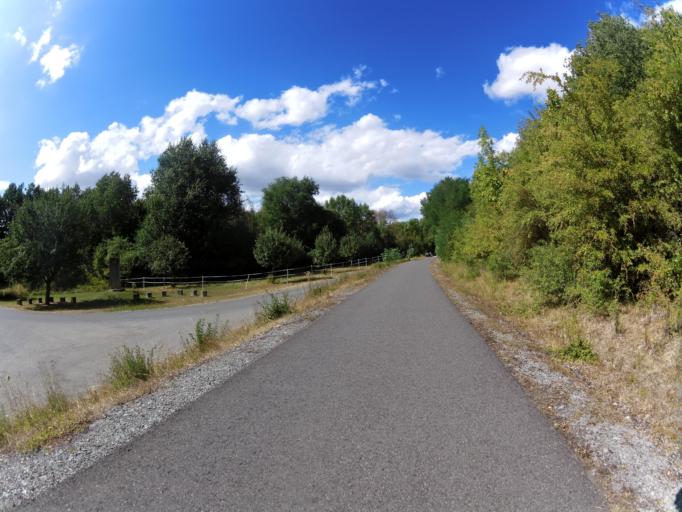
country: DE
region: Bavaria
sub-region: Regierungsbezirk Unterfranken
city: Gaukonigshofen
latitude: 49.6264
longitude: 10.0081
